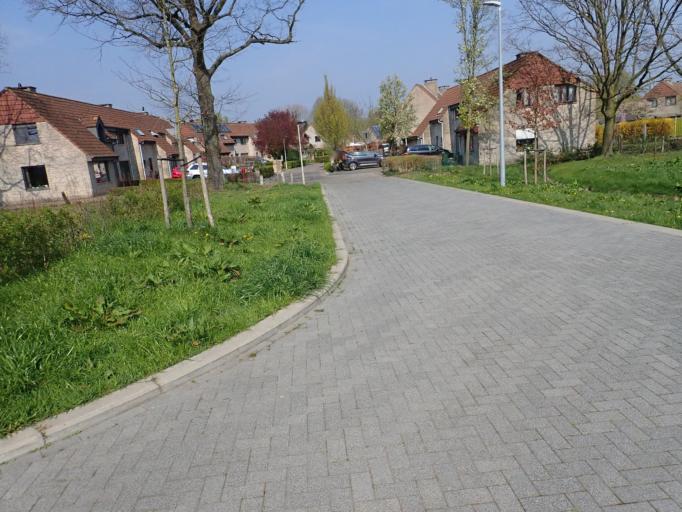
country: BE
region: Flanders
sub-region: Provincie Antwerpen
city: Kalmthout
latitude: 51.3865
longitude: 4.4683
